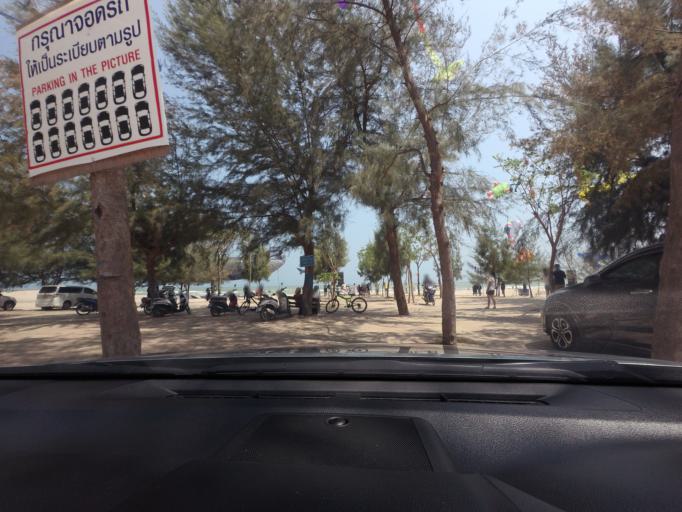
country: TH
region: Phetchaburi
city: Cha-am
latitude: 12.8099
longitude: 99.9905
